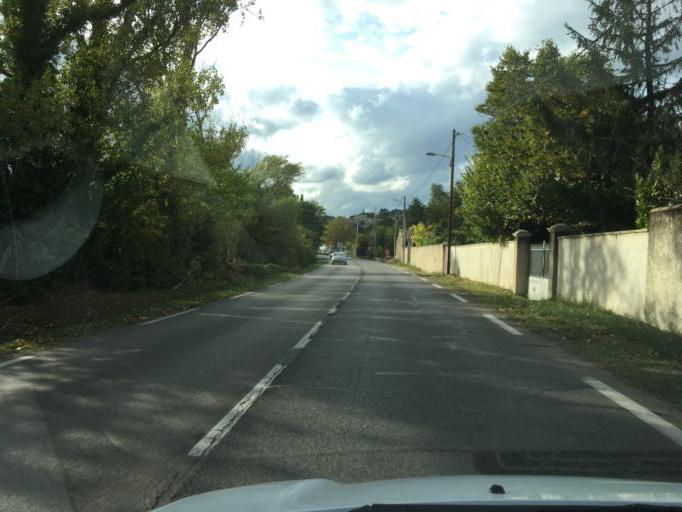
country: FR
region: Provence-Alpes-Cote d'Azur
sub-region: Departement du Vaucluse
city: Chateauneuf-de-Gadagne
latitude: 43.9267
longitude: 4.9542
